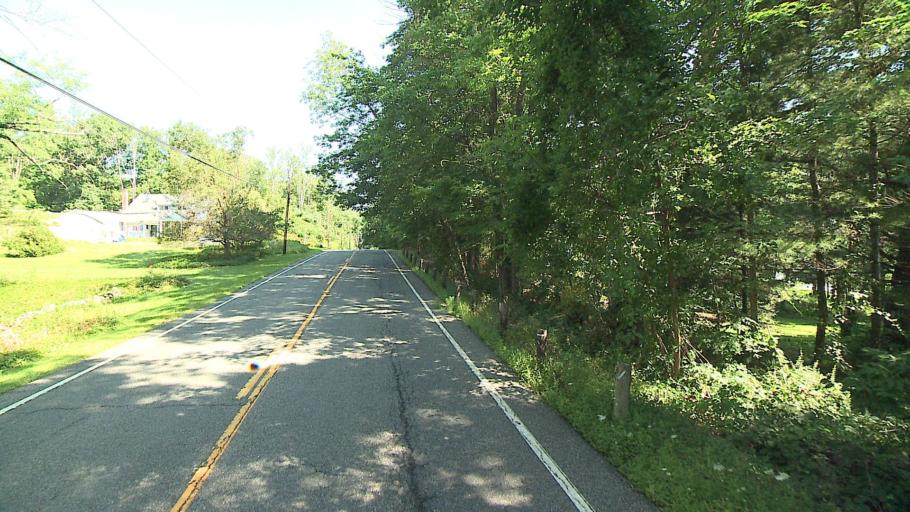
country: US
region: Connecticut
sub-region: Litchfield County
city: Canaan
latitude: 42.0325
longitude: -73.4283
